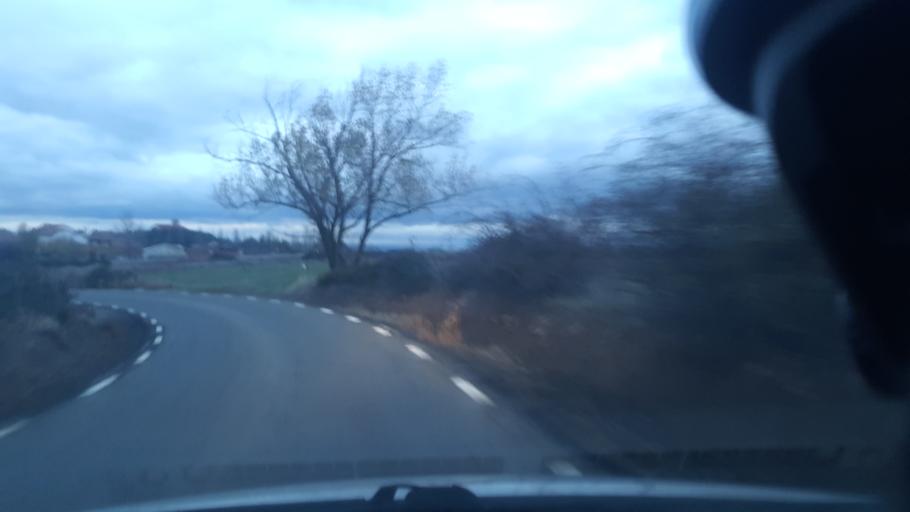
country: ES
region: Castille and Leon
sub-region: Provincia de Avila
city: Ojos-Albos
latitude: 40.7407
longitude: -4.4714
